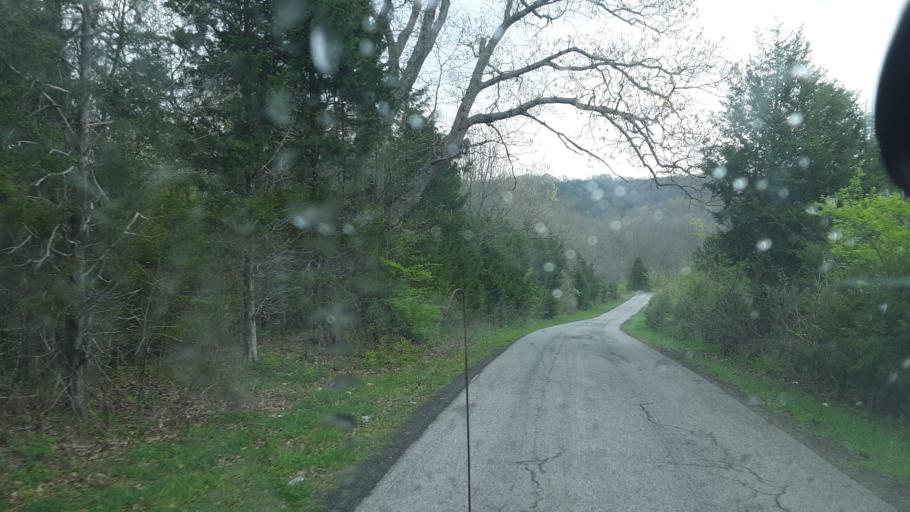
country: US
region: Kentucky
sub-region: Owen County
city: Owenton
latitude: 38.6756
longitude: -84.8009
